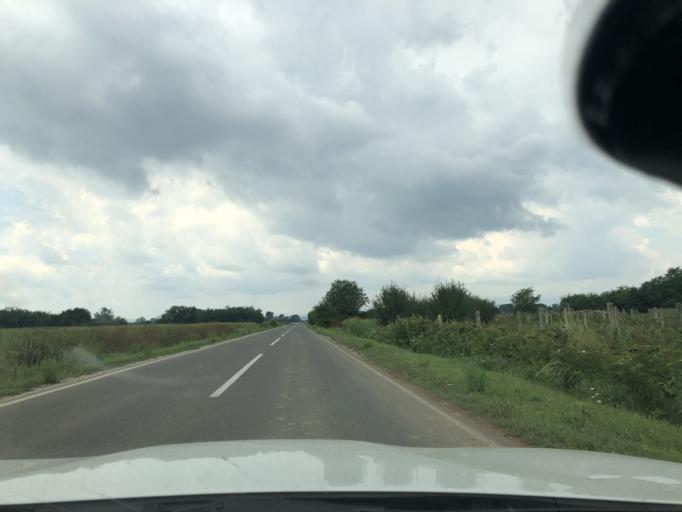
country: RS
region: Central Serbia
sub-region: Jablanicki Okrug
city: Leskovac
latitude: 42.9688
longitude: 21.8709
